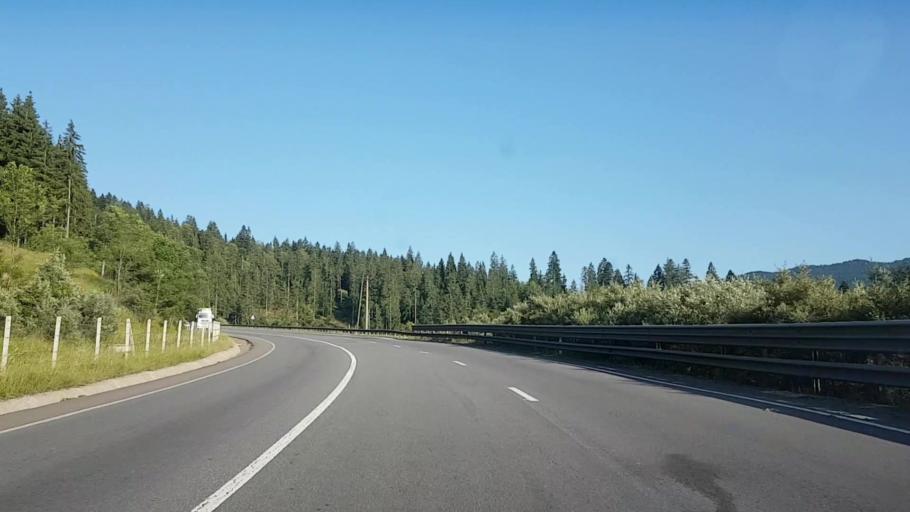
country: RO
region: Bistrita-Nasaud
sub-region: Comuna Lunca Ilvei
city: Lunca Ilvei
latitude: 47.2284
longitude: 24.9677
